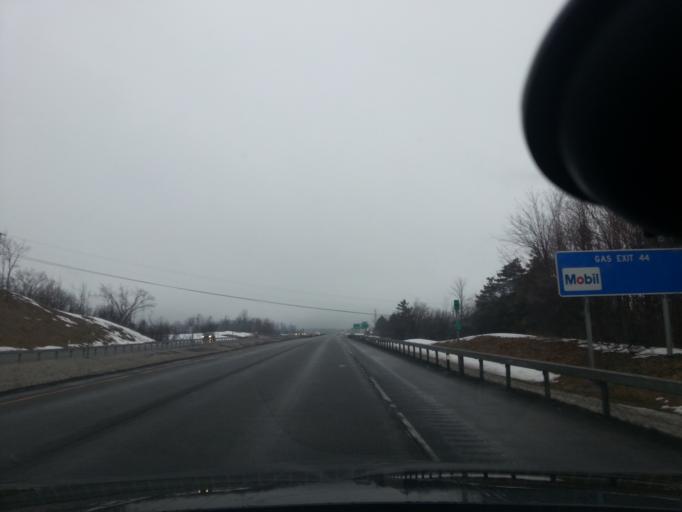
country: US
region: New York
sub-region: Jefferson County
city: Adams Center
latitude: 43.9187
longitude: -75.9750
